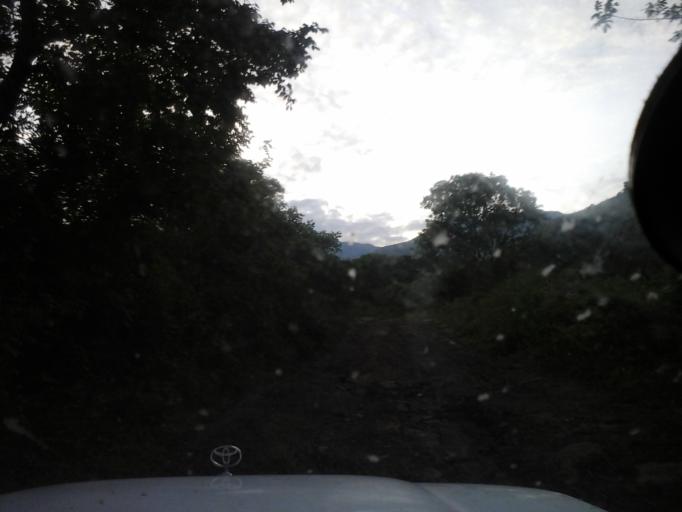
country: CO
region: Cesar
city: Agustin Codazzi
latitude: 10.1731
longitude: -73.1547
